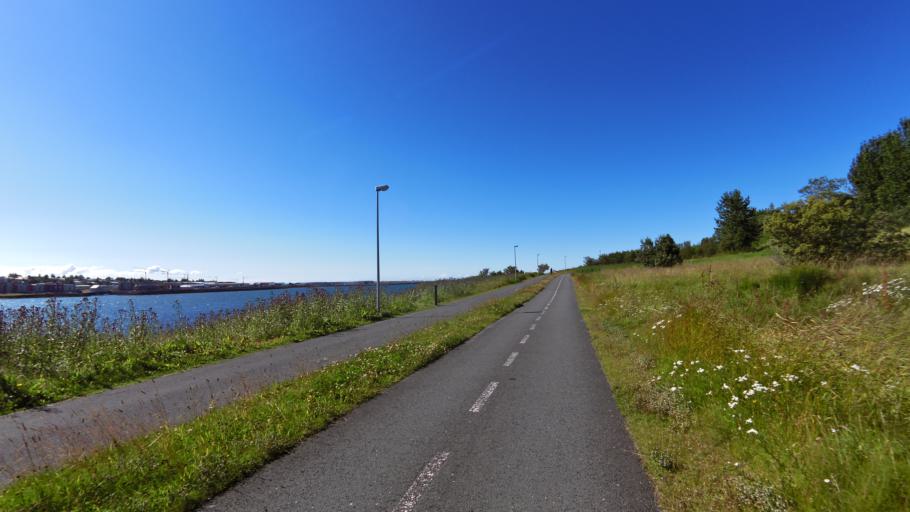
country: IS
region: Capital Region
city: Kopavogur
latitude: 64.1210
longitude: -21.9123
